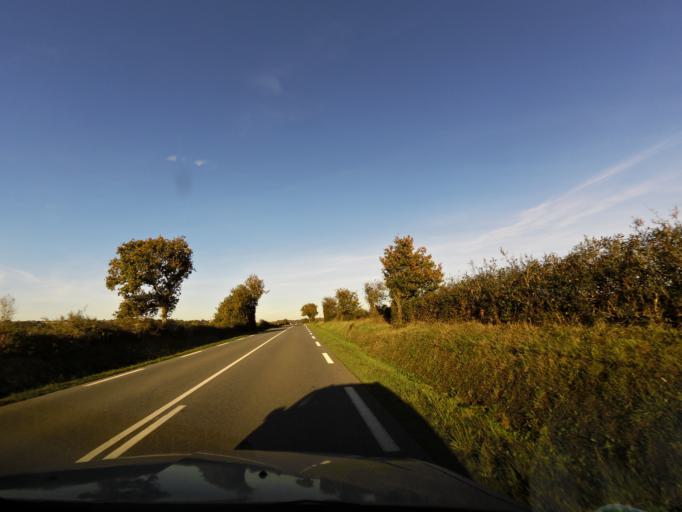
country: FR
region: Brittany
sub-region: Departement d'Ille-et-Vilaine
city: Pance
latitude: 47.8662
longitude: -1.6605
